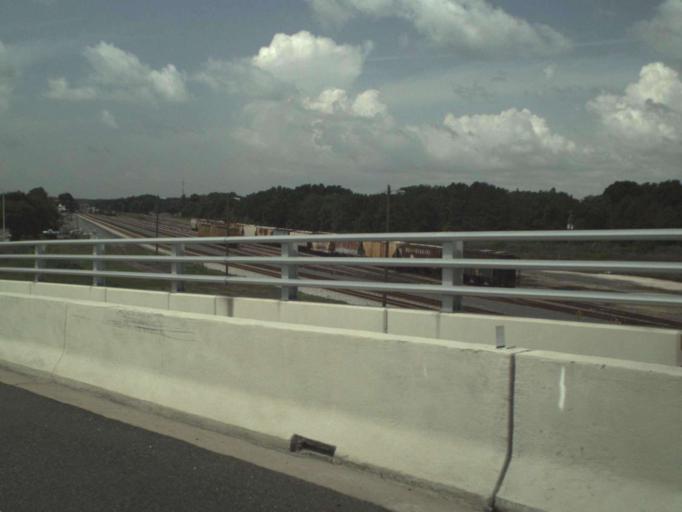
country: US
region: Florida
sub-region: Sumter County
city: Wildwood
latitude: 28.8728
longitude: -82.0365
